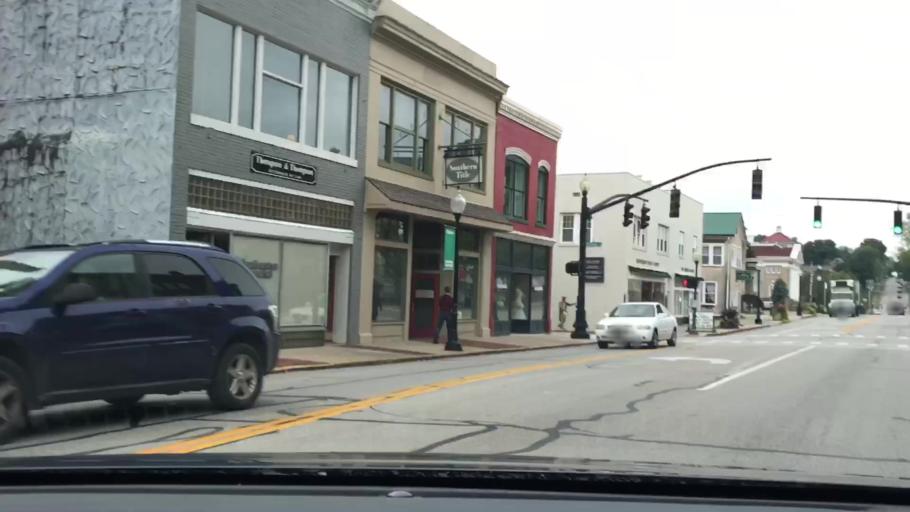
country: US
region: Kentucky
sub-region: Pulaski County
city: Somerset
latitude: 37.0924
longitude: -84.6048
